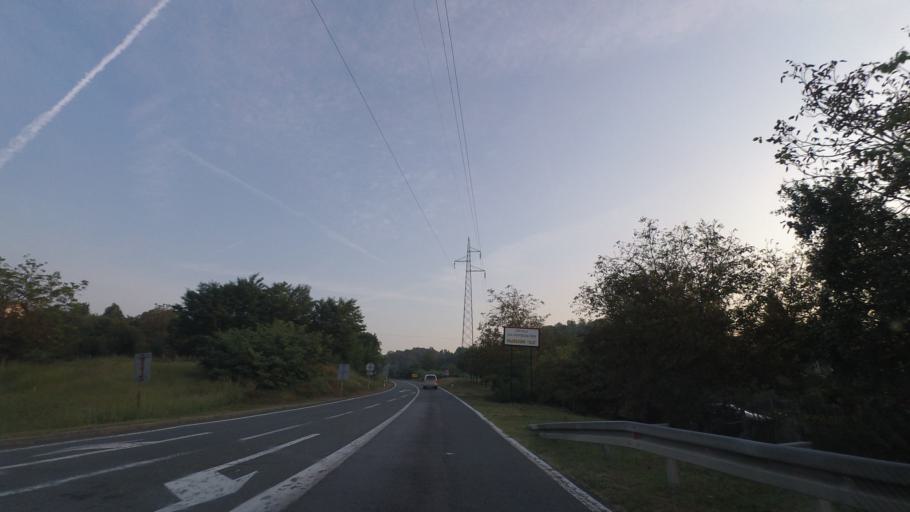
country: HR
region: Brodsko-Posavska
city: Nova Gradiska
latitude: 45.2573
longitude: 17.4100
